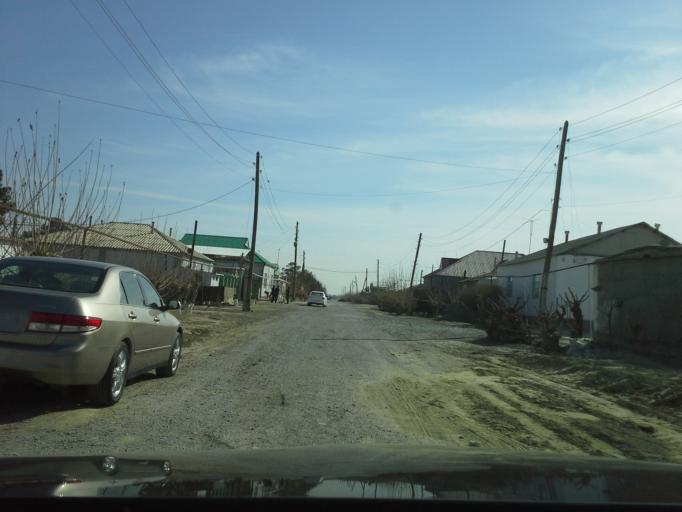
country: TM
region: Ahal
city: Abadan
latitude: 38.1243
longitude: 57.9987
